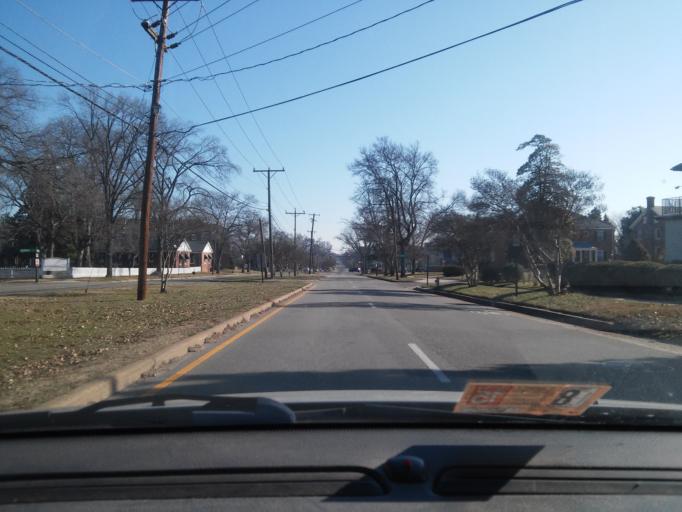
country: US
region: Virginia
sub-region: City of Richmond
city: Richmond
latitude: 37.5723
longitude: -77.4478
